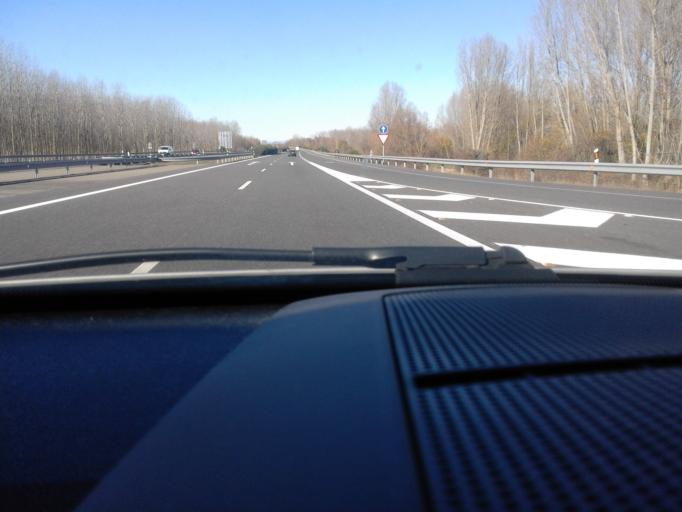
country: ES
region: Castille and Leon
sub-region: Provincia de Leon
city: Campo de Villavidel
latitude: 42.4561
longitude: -5.5212
